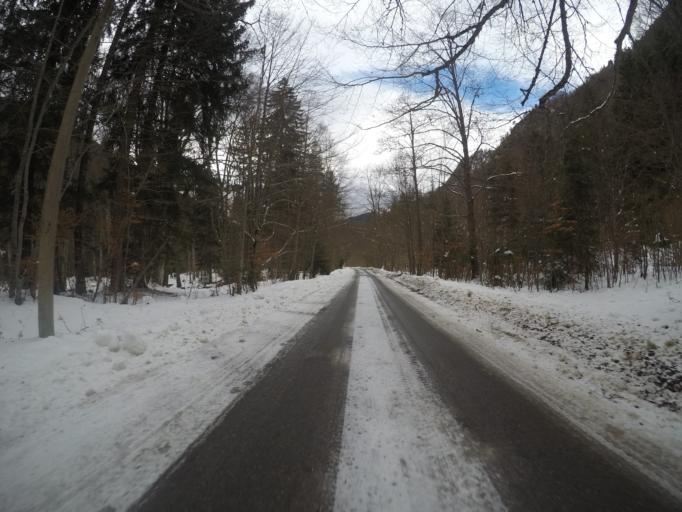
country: BG
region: Kyustendil
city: Sapareva Banya
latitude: 42.1487
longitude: 23.3725
